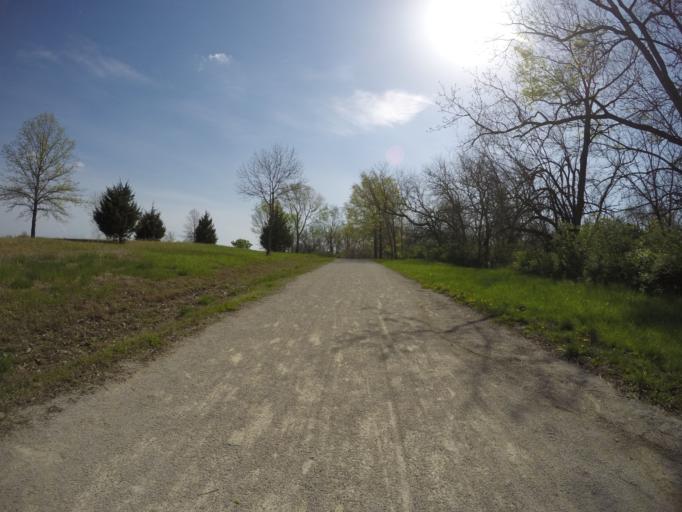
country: US
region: Missouri
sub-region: Jackson County
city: Grandview
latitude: 38.9107
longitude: -94.4778
